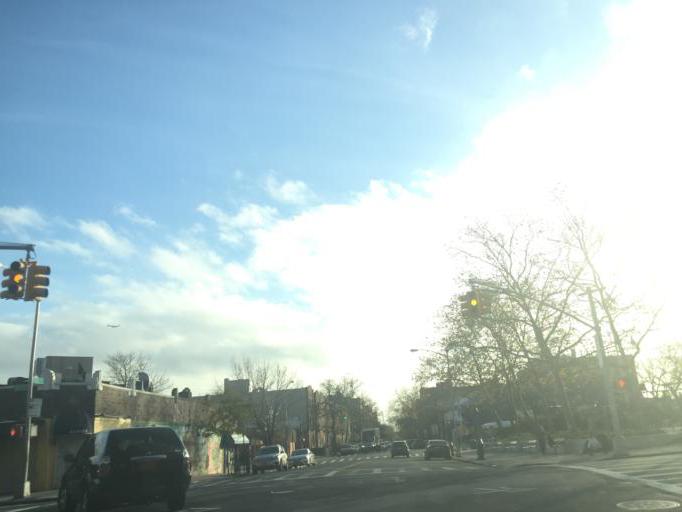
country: US
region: New York
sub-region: Queens County
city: Long Island City
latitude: 40.7417
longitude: -73.9219
